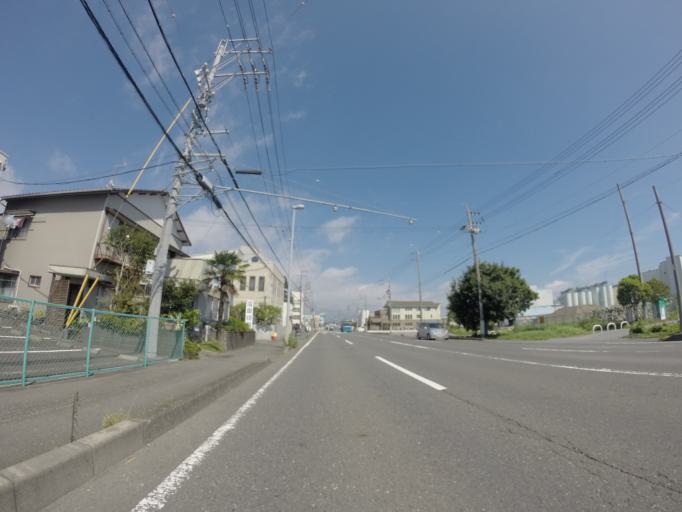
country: JP
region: Shizuoka
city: Shizuoka-shi
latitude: 34.9911
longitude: 138.4961
